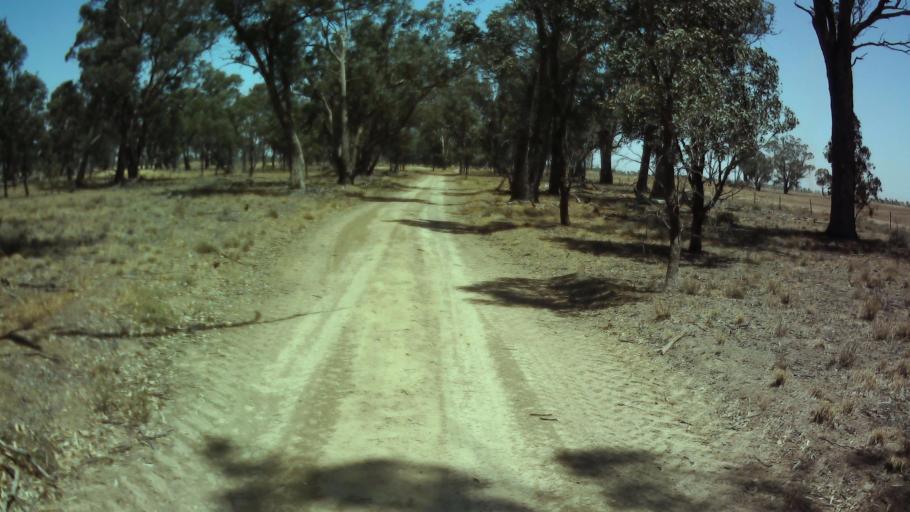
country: AU
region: New South Wales
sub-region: Weddin
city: Grenfell
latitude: -34.0508
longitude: 147.8289
